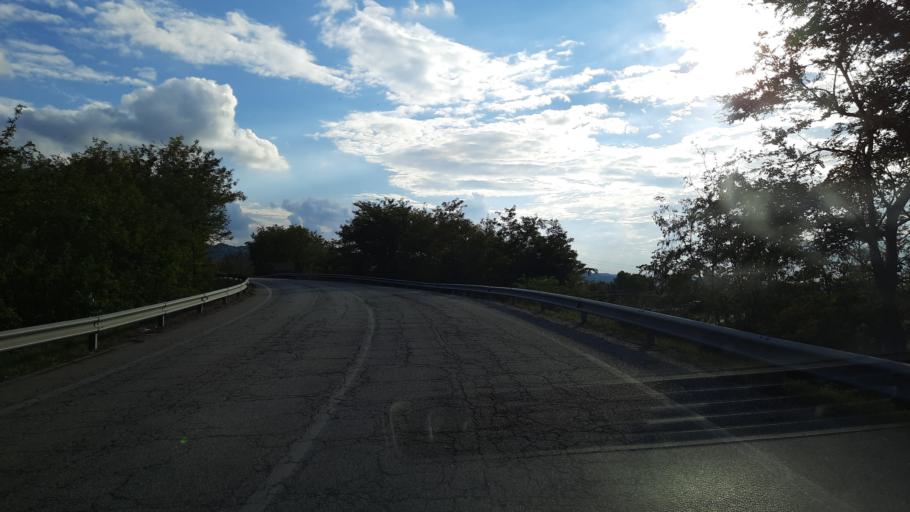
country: IT
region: Piedmont
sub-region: Provincia di Vercelli
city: Palazzolo Vercellese
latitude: 45.1928
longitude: 8.2588
